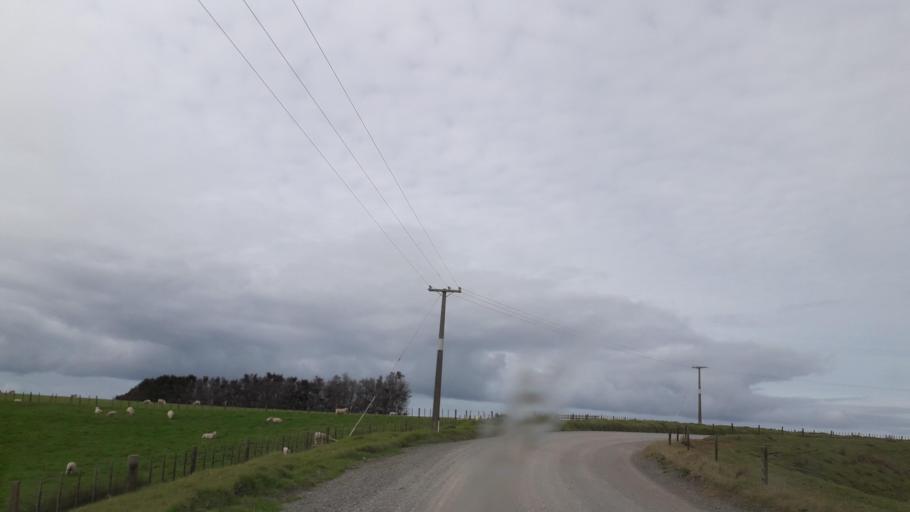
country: NZ
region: Northland
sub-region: Far North District
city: Kerikeri
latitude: -35.1287
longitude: 174.0080
